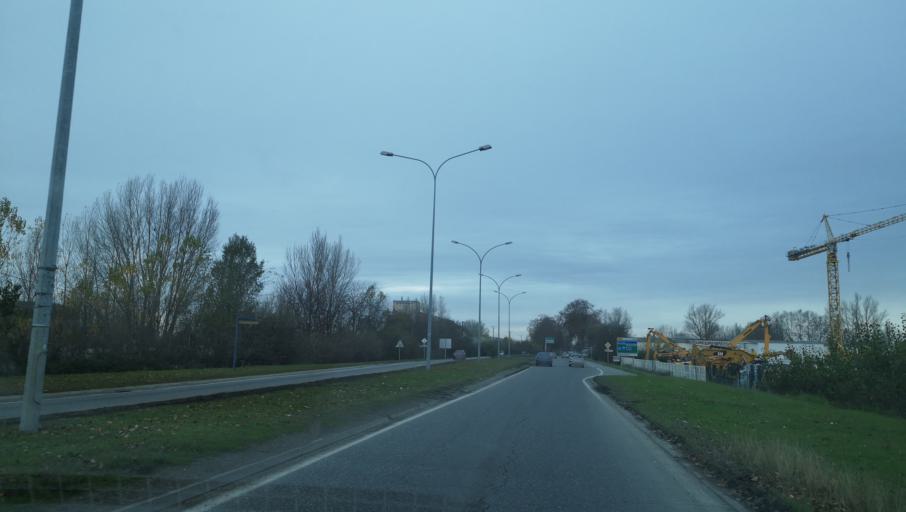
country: FR
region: Midi-Pyrenees
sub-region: Departement de la Haute-Garonne
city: Lespinasse
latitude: 43.7110
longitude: 1.3906
